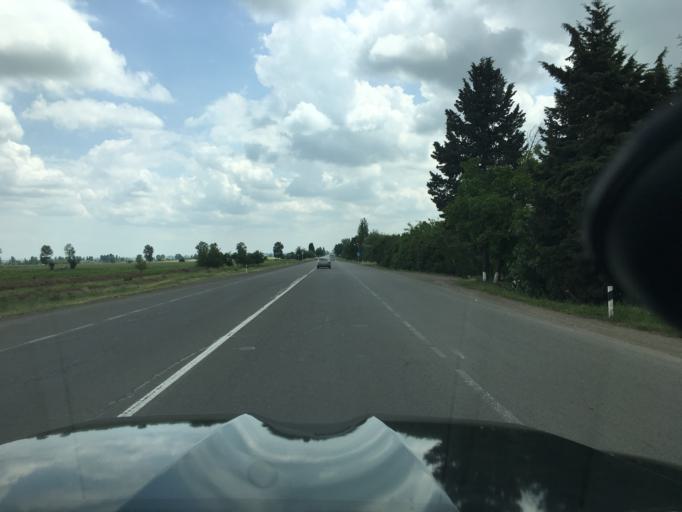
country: AZ
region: Tovuz
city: Tovuz
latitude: 40.9586
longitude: 45.7270
